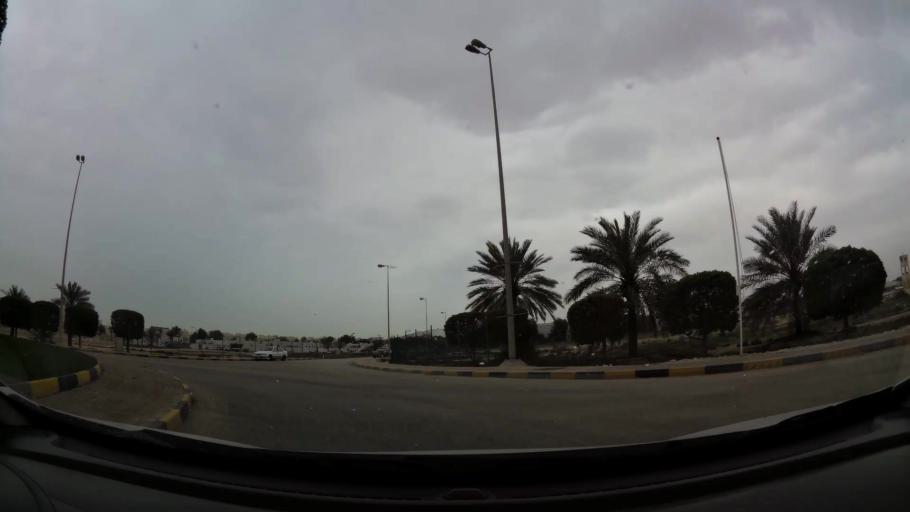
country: BH
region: Northern
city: Ar Rifa'
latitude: 26.1072
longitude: 50.5362
